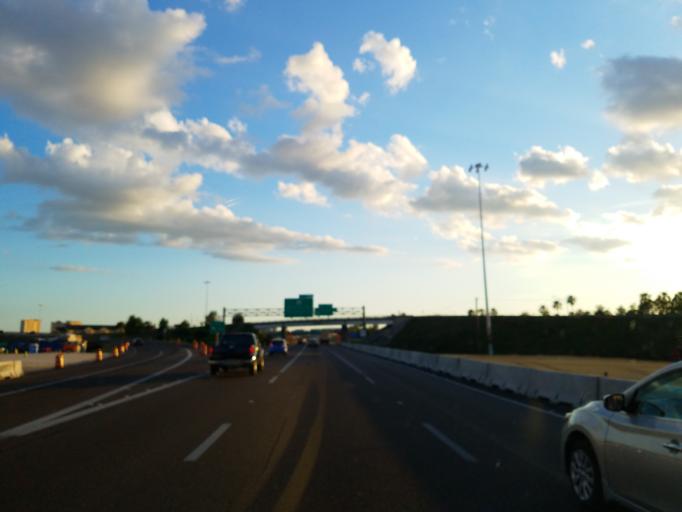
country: US
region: Florida
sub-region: Orange County
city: Tangelo Park
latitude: 28.4707
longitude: -81.4594
